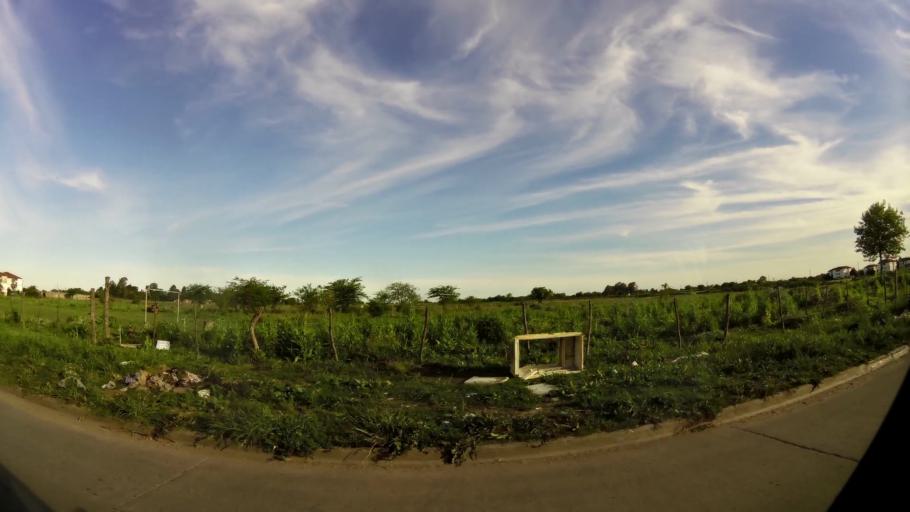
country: AR
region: Buenos Aires
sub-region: Partido de Almirante Brown
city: Adrogue
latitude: -34.8183
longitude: -58.3358
